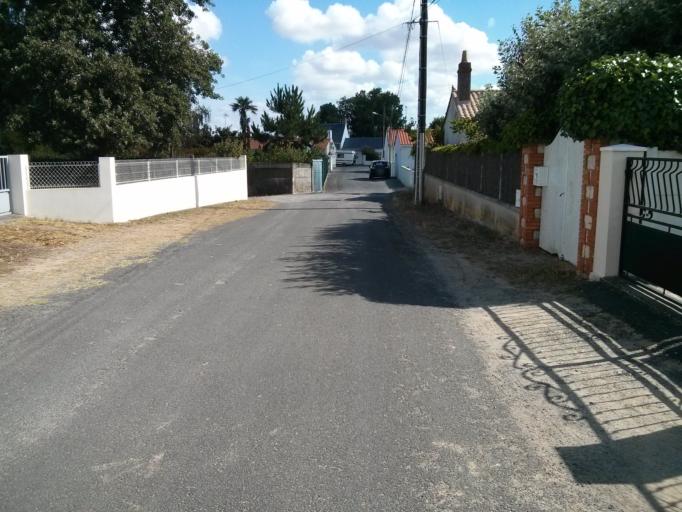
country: FR
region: Pays de la Loire
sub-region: Departement de la Vendee
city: Saint-Jean-de-Monts
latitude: 46.7946
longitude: -2.0690
